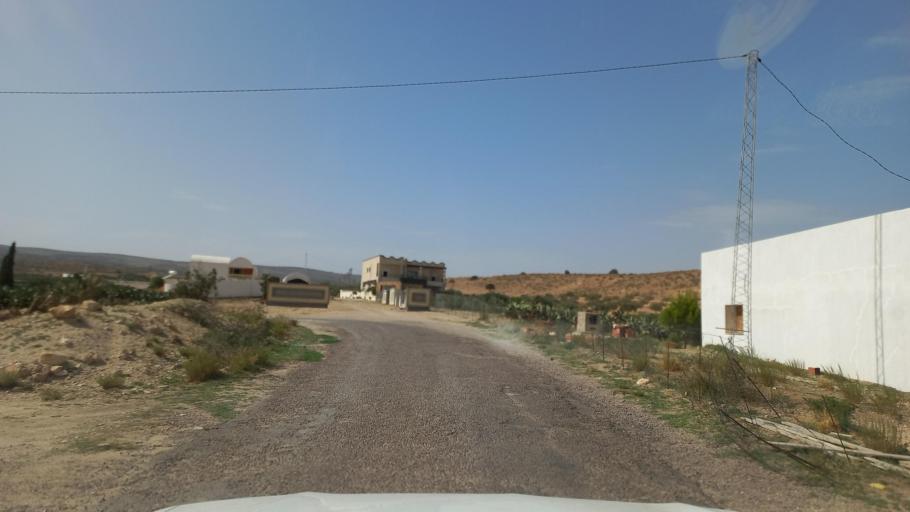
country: TN
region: Al Qasrayn
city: Kasserine
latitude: 35.3028
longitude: 8.9500
